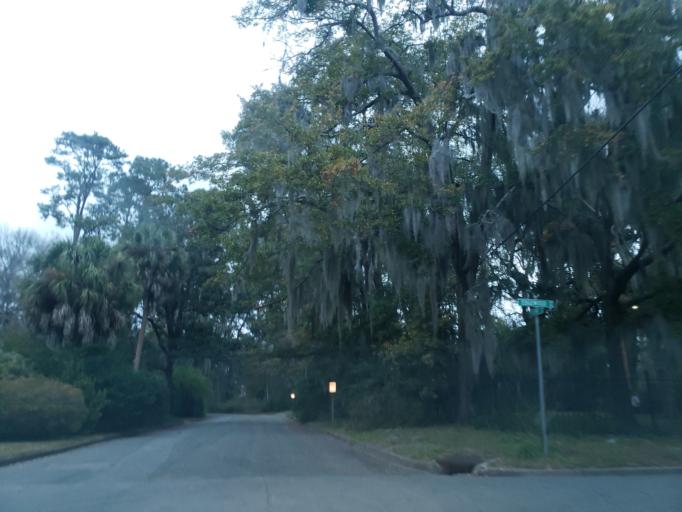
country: US
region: Georgia
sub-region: Chatham County
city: Thunderbolt
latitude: 32.0565
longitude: -81.0675
